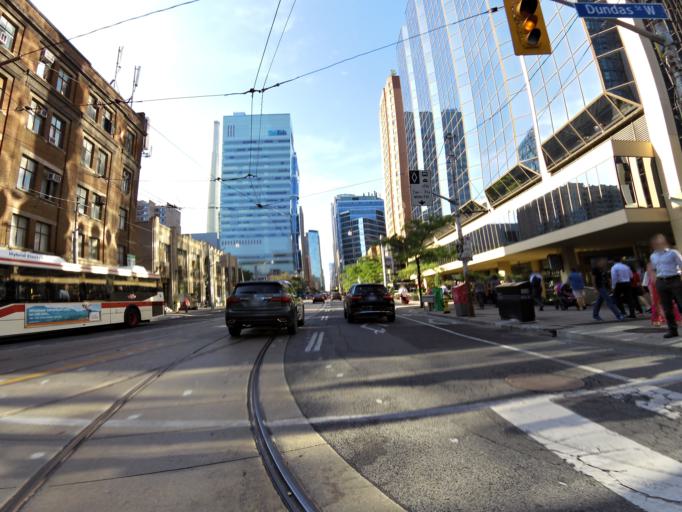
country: CA
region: Ontario
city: Toronto
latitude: 43.6497
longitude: -79.3832
